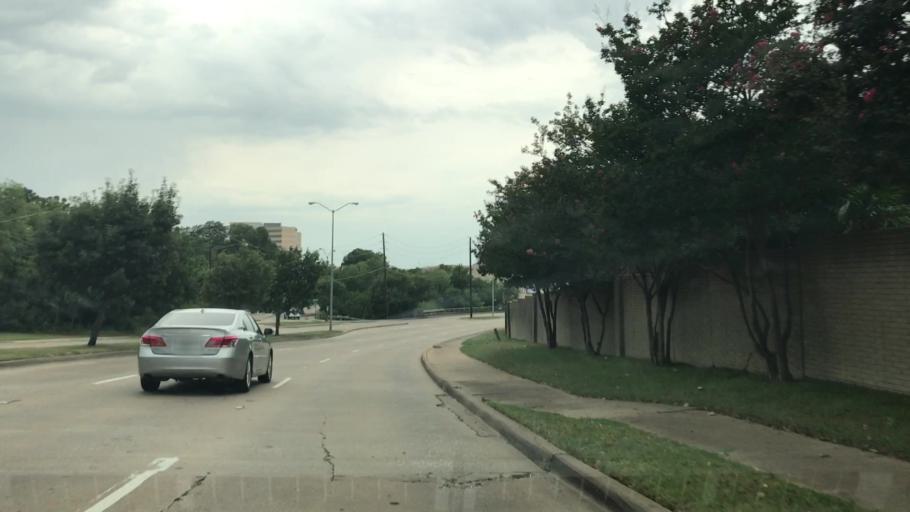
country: US
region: Texas
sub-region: Dallas County
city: Addison
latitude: 32.9499
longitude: -96.7972
